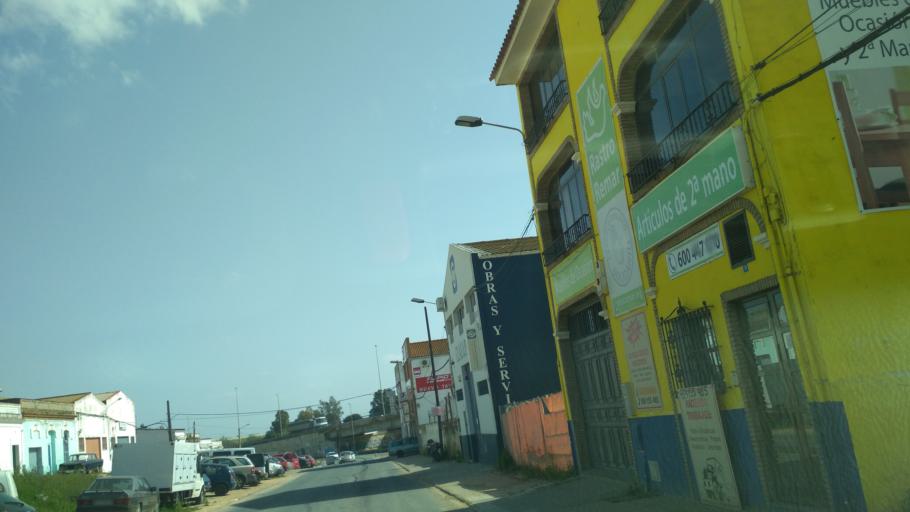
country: ES
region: Andalusia
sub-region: Provincia de Huelva
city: Huelva
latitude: 37.2526
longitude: -6.9345
